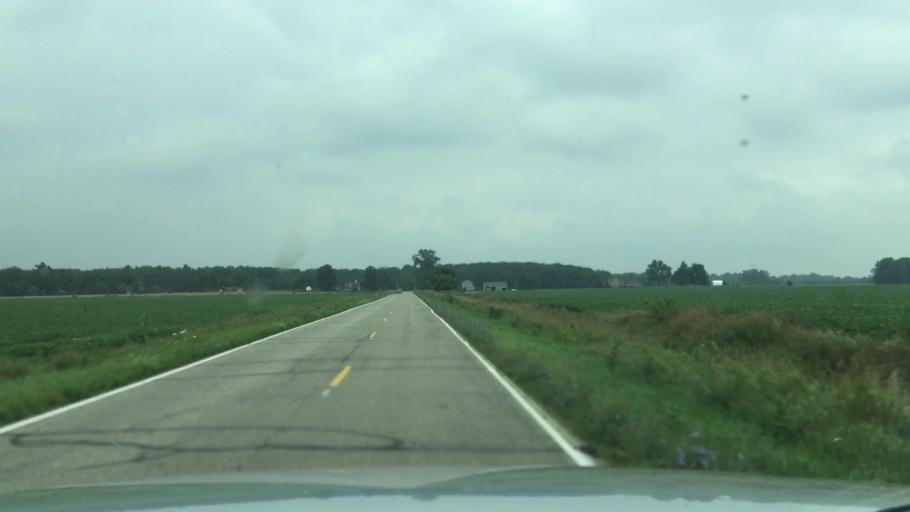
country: US
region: Michigan
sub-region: Shiawassee County
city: New Haven
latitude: 43.0637
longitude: -84.2261
